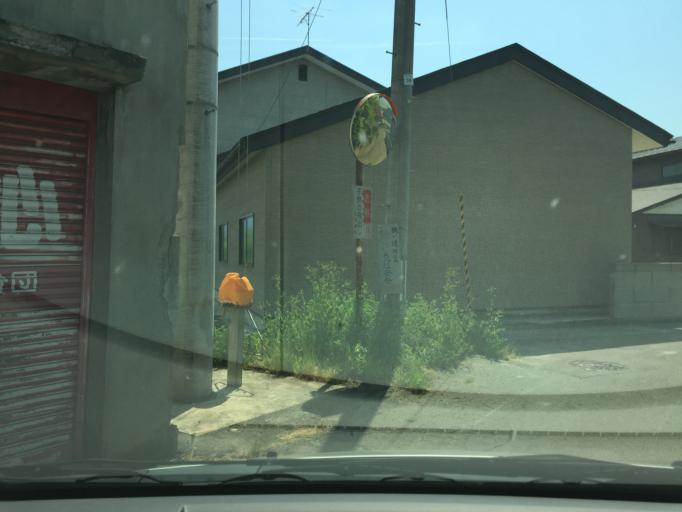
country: JP
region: Fukushima
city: Kitakata
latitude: 37.4645
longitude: 139.8980
